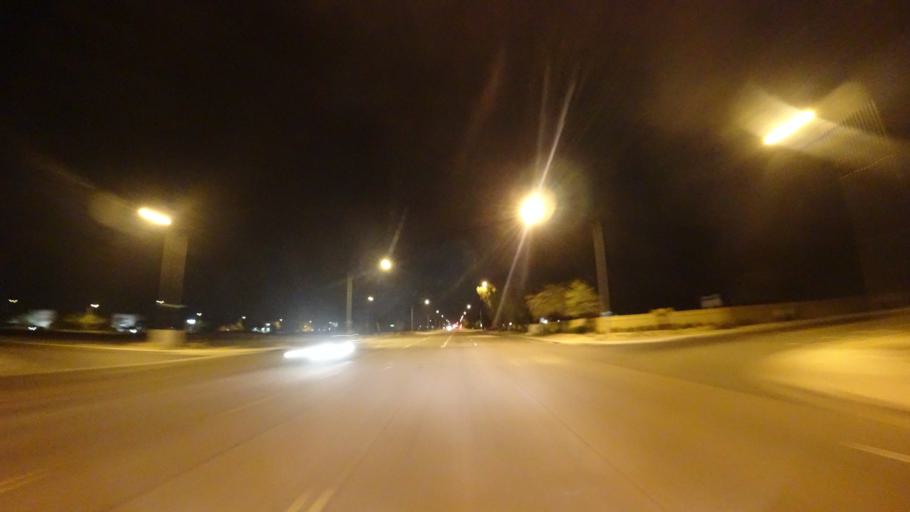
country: US
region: Arizona
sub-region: Maricopa County
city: Mesa
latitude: 33.4444
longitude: -111.7188
